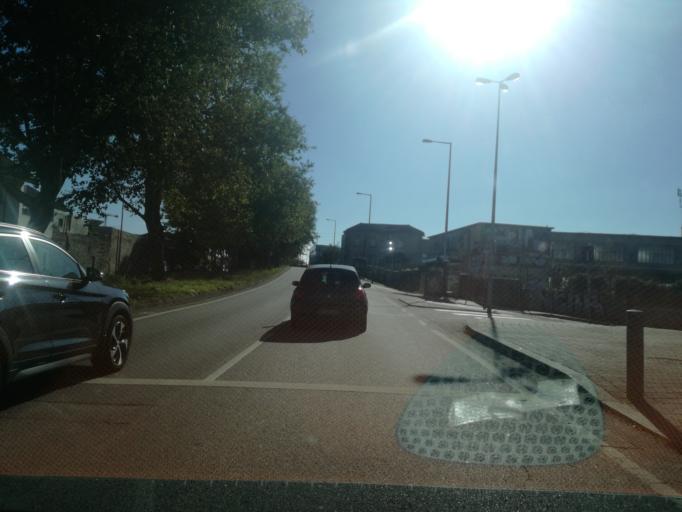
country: PT
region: Porto
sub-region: Matosinhos
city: Sao Mamede de Infesta
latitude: 41.1845
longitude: -8.6097
